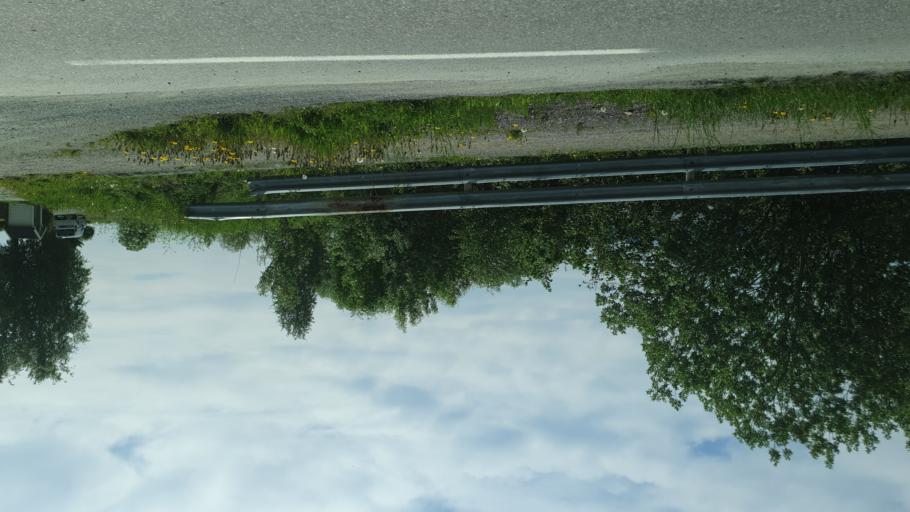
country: NO
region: Nord-Trondelag
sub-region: Leksvik
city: Leksvik
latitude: 63.6833
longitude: 10.5952
